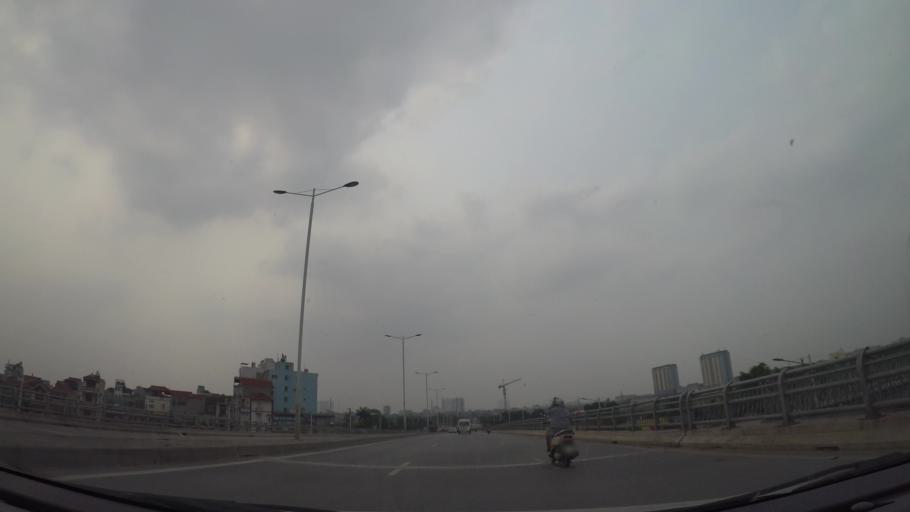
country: VN
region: Ha Noi
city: Cau Dien
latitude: 21.0346
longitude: 105.7520
